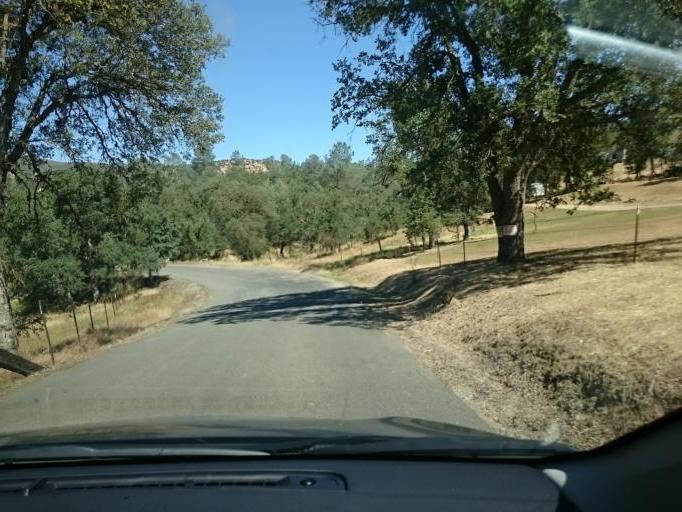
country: US
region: California
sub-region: Calaveras County
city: Rancho Calaveras
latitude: 38.1122
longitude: -120.7800
